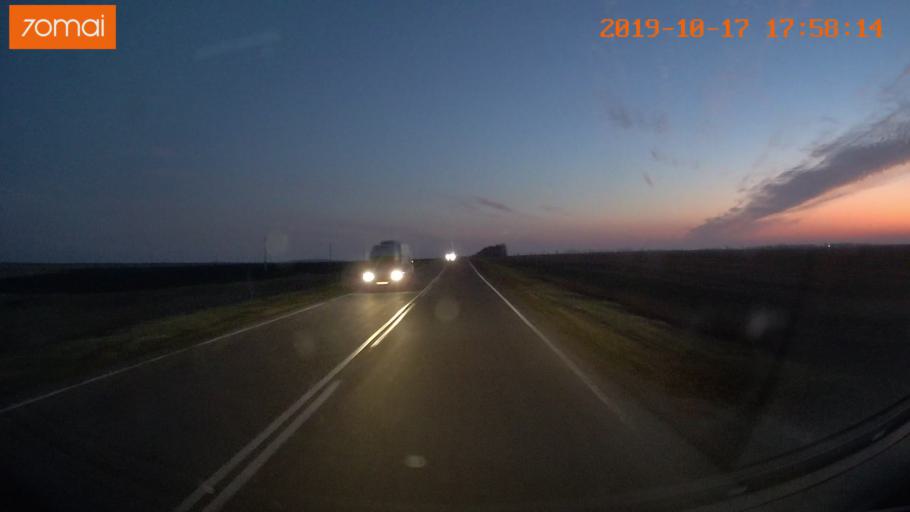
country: RU
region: Tula
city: Kurkino
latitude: 53.5579
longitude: 38.6293
